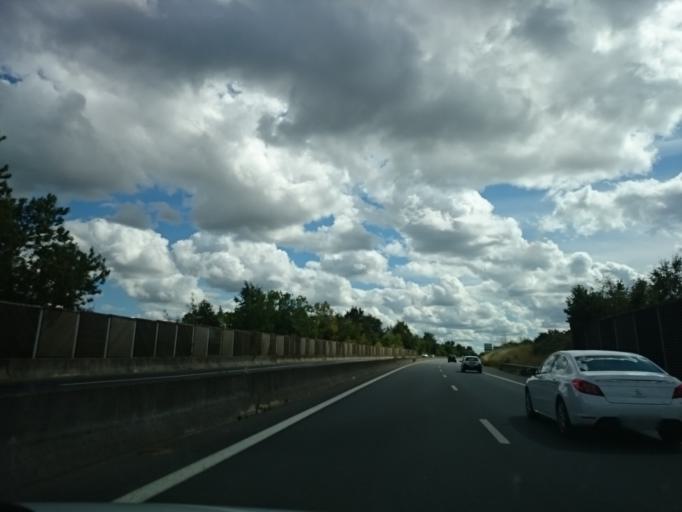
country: FR
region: Pays de la Loire
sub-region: Departement de la Loire-Atlantique
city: Sainte-Luce-sur-Loire
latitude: 47.2486
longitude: -1.4758
